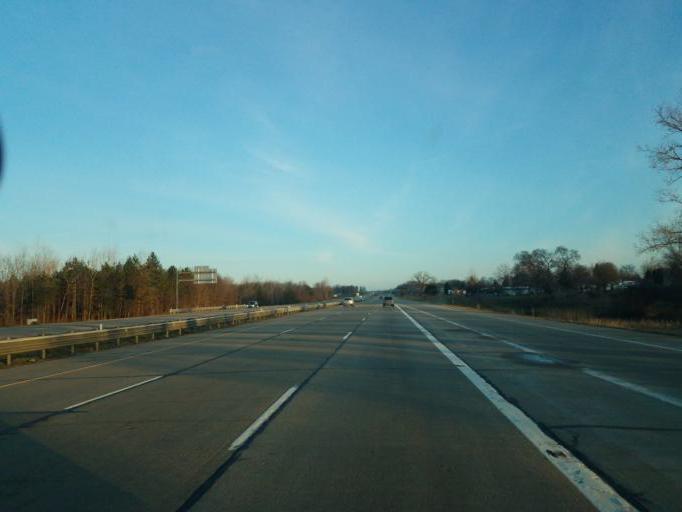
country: US
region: Michigan
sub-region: Livingston County
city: Howell
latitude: 42.5930
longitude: -83.9371
